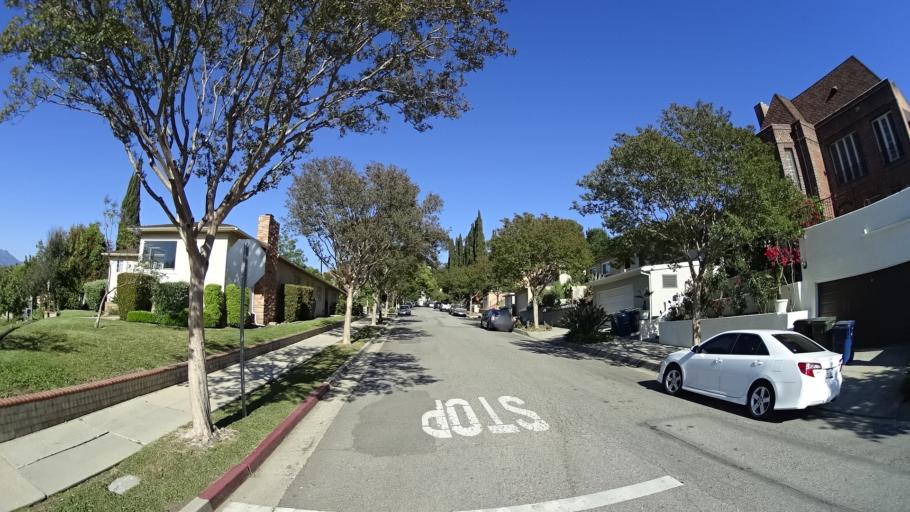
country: US
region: California
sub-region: Los Angeles County
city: Belvedere
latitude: 34.0740
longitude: -118.1581
